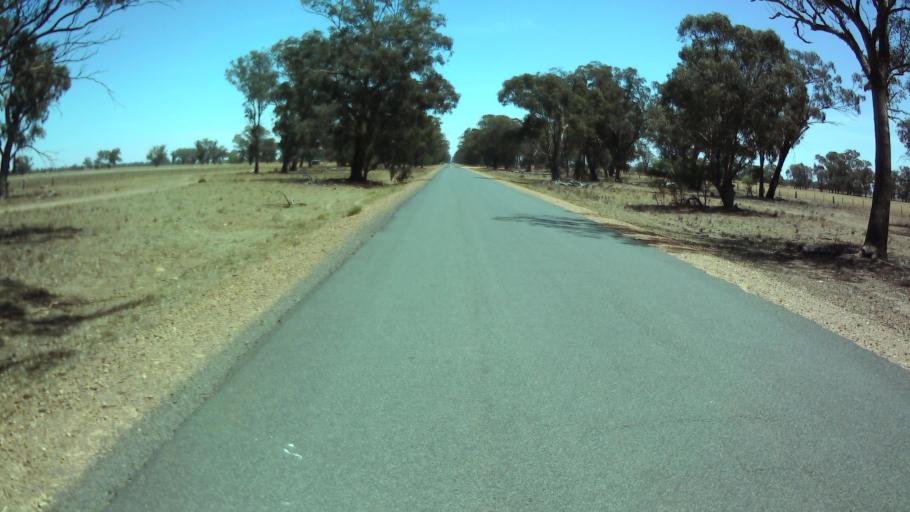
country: AU
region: New South Wales
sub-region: Weddin
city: Grenfell
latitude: -34.0326
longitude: 147.9031
